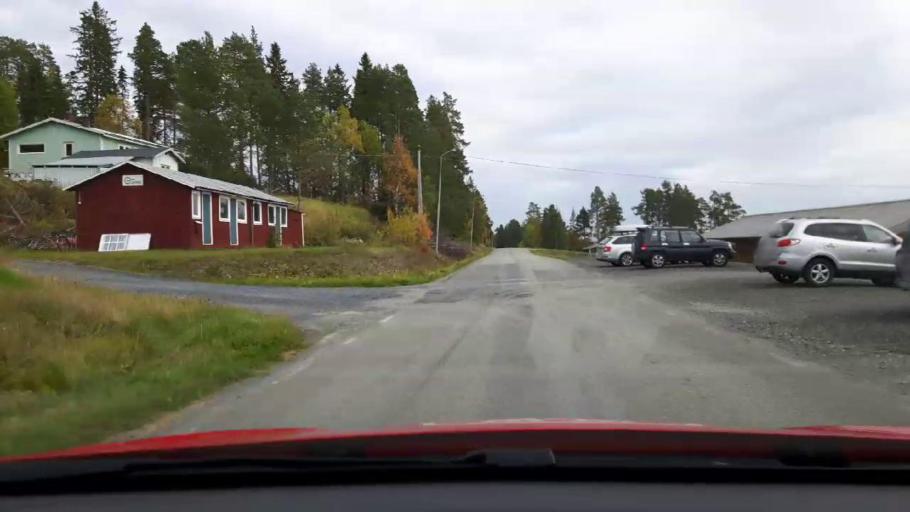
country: SE
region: Jaemtland
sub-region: Krokoms Kommun
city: Valla
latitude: 63.2585
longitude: 14.0152
